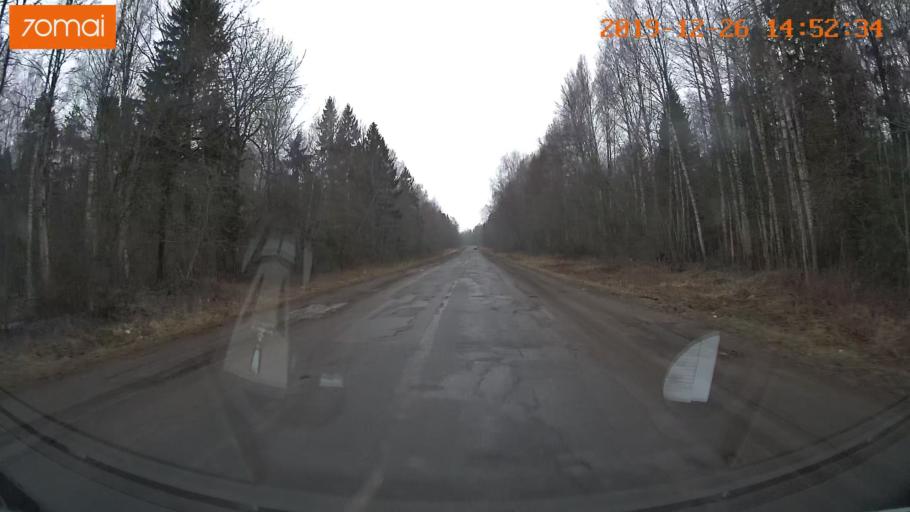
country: RU
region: Jaroslavl
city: Rybinsk
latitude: 58.3208
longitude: 38.8974
